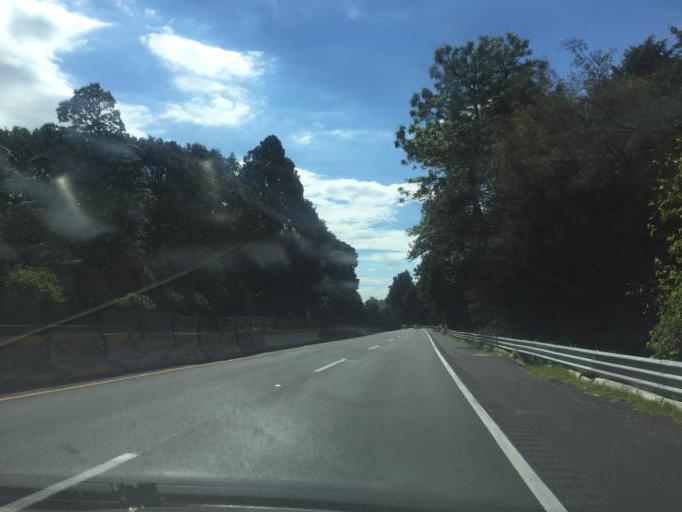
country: MX
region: Morelos
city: Tres Marias
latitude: 19.0382
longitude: -99.2285
